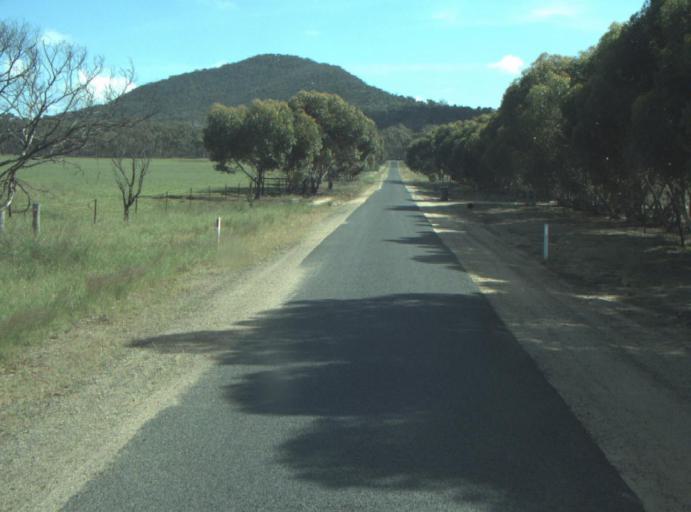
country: AU
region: Victoria
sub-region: Greater Geelong
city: Lara
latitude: -37.9729
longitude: 144.4241
